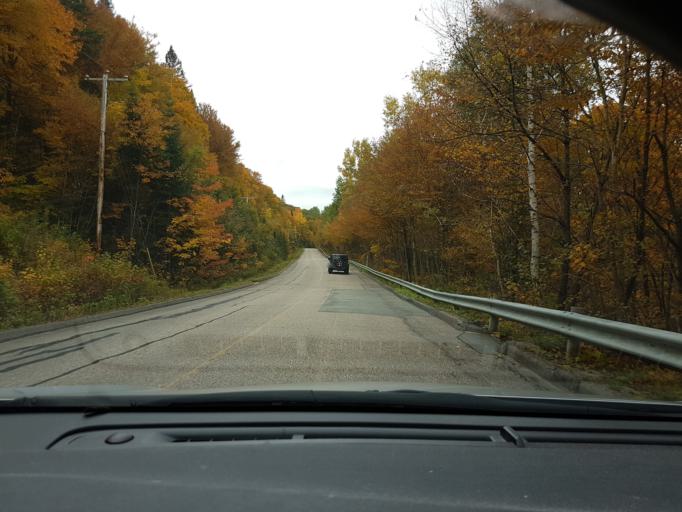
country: CA
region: Quebec
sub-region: Capitale-Nationale
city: Shannon
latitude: 47.1107
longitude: -71.3568
